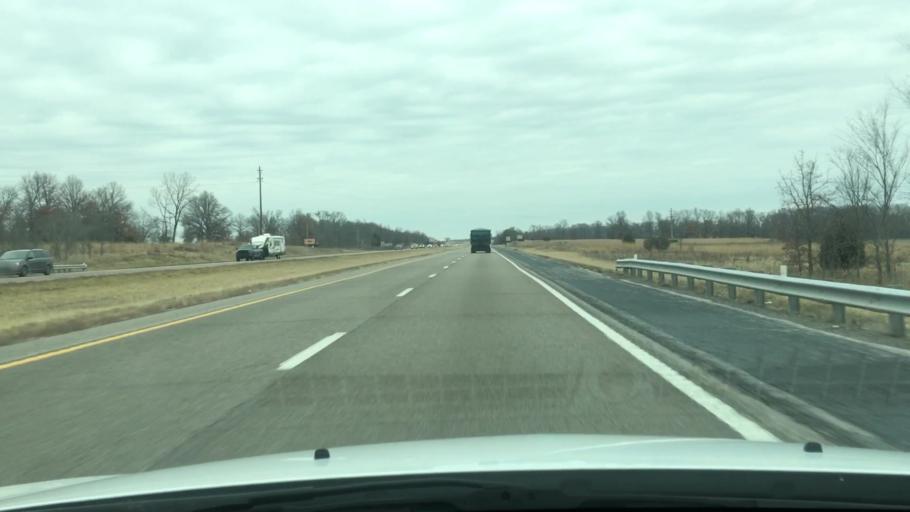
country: US
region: Missouri
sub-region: Audrain County
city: Mexico
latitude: 39.0491
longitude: -91.8938
